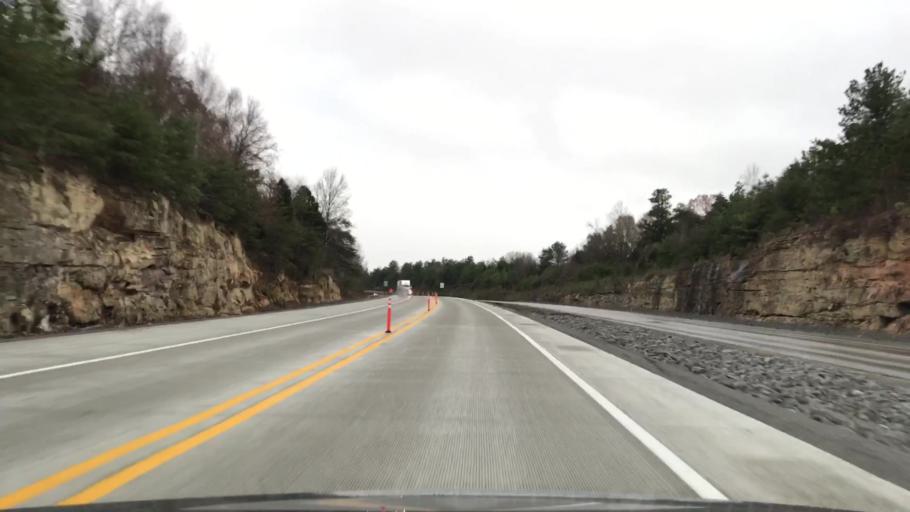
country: US
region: Kentucky
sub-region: Christian County
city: Hopkinsville
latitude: 36.9966
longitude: -87.4658
